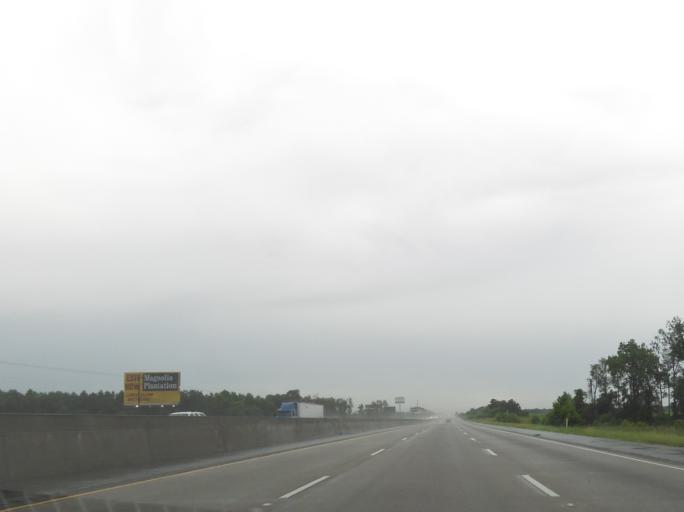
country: US
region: Georgia
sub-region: Tift County
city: Unionville
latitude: 31.3902
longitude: -83.4982
